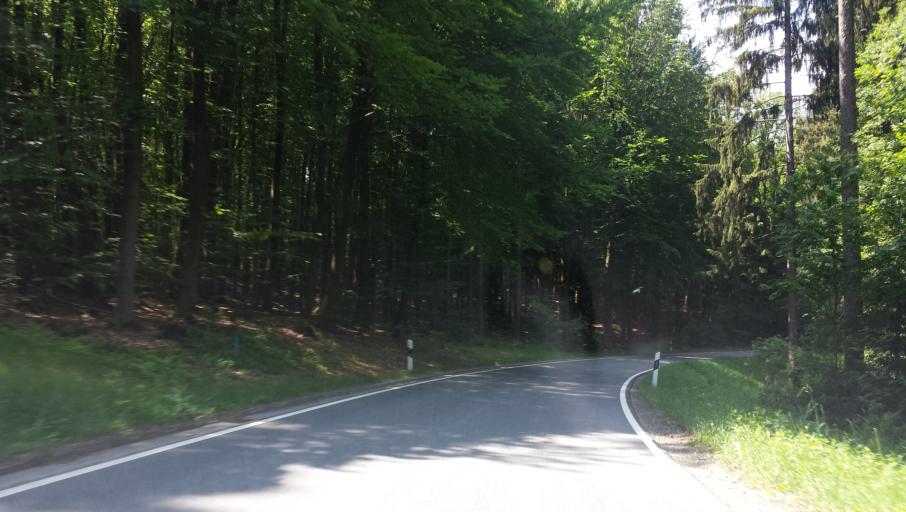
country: DE
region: Hesse
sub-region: Regierungsbezirk Darmstadt
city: Beerfelden
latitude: 49.5464
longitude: 8.9447
